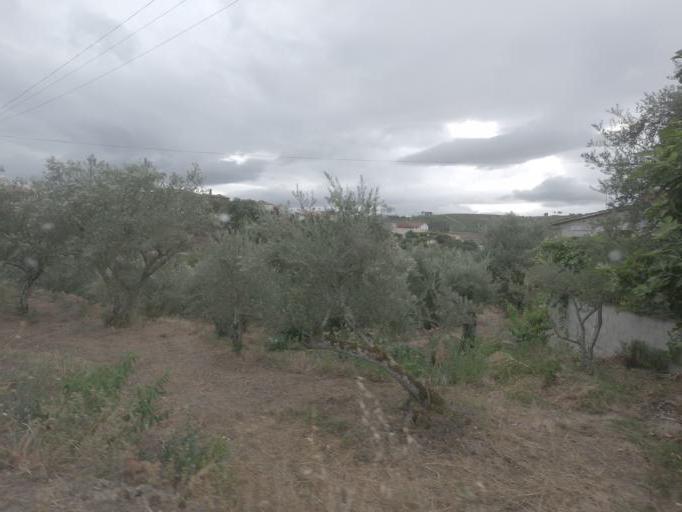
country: PT
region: Vila Real
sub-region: Sabrosa
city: Sabrosa
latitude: 41.2248
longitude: -7.5022
